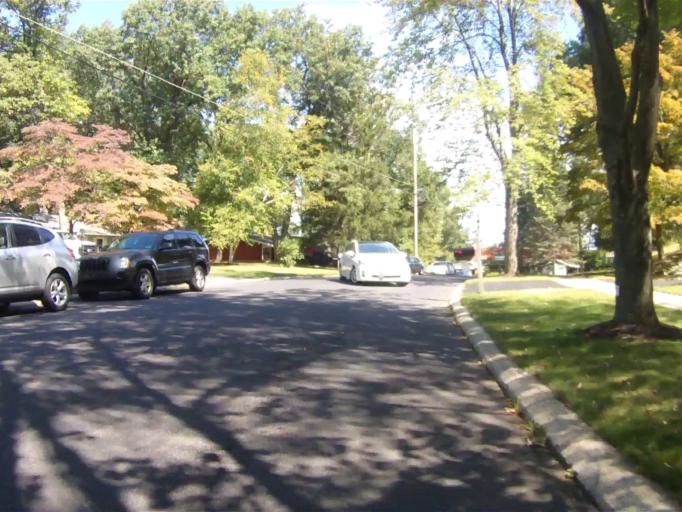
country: US
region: Pennsylvania
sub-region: Centre County
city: Park Forest Village
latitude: 40.8083
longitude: -77.9120
